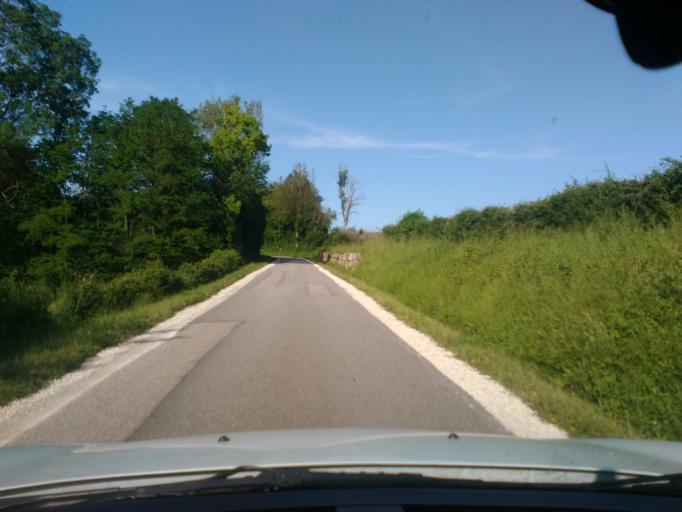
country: FR
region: Lorraine
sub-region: Departement des Vosges
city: Mirecourt
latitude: 48.2781
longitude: 6.1553
